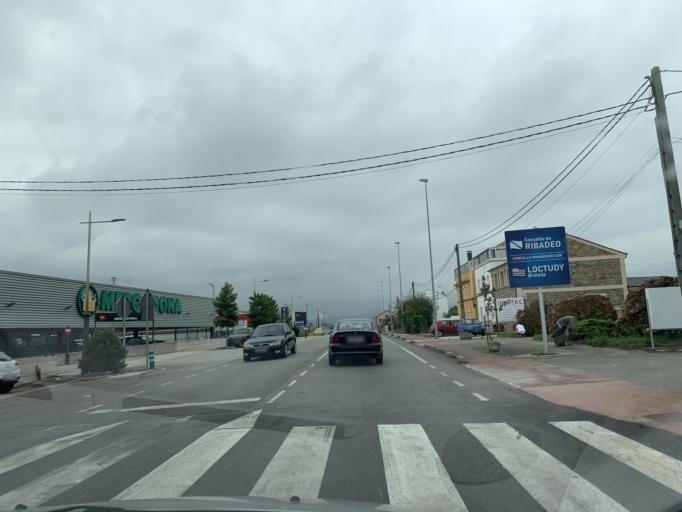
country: ES
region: Galicia
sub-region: Provincia de Lugo
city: Ribadeo
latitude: 43.5402
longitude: -7.0641
